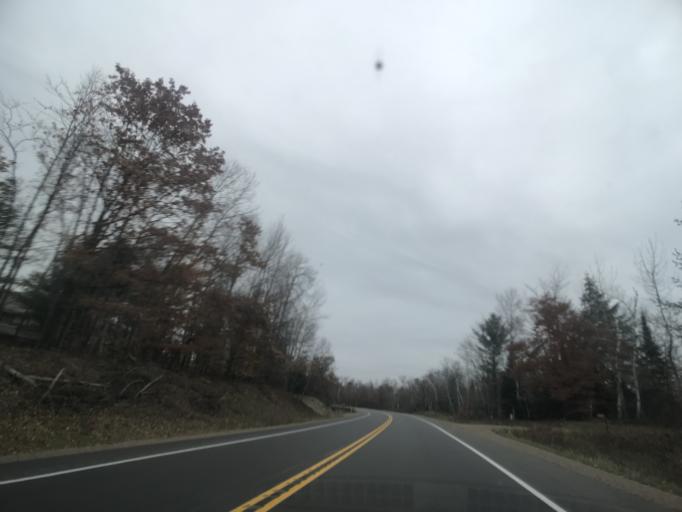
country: US
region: Wisconsin
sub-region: Menominee County
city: Legend Lake
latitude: 45.2702
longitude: -88.5092
